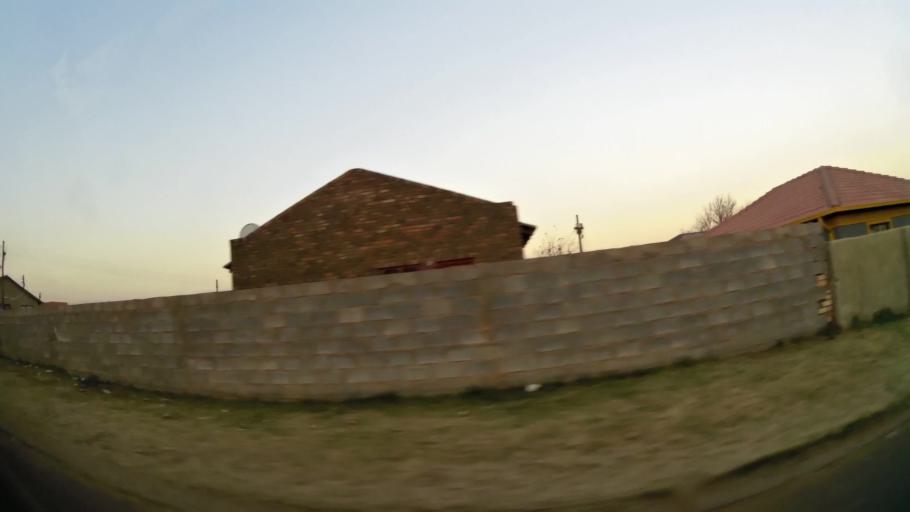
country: ZA
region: Gauteng
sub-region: West Rand District Municipality
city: Randfontein
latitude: -26.2095
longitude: 27.7114
